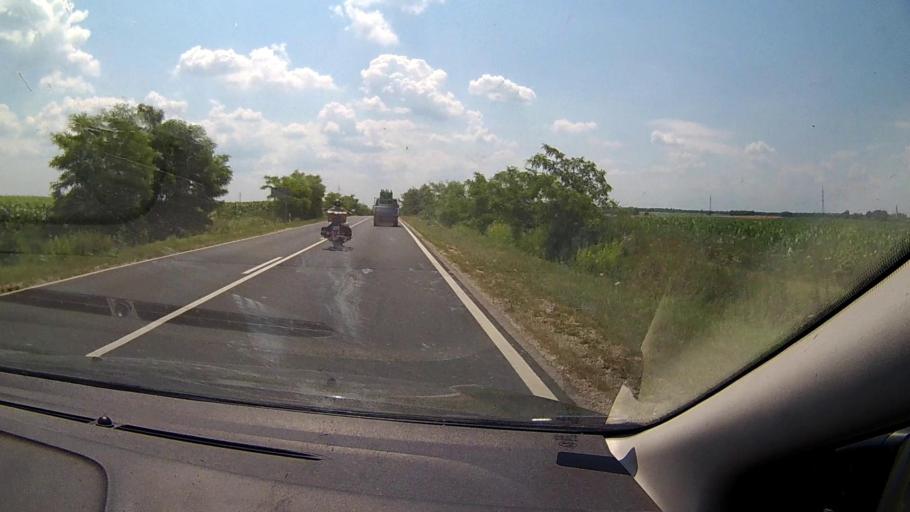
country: HU
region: Komarom-Esztergom
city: Tata
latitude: 47.6177
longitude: 18.3165
